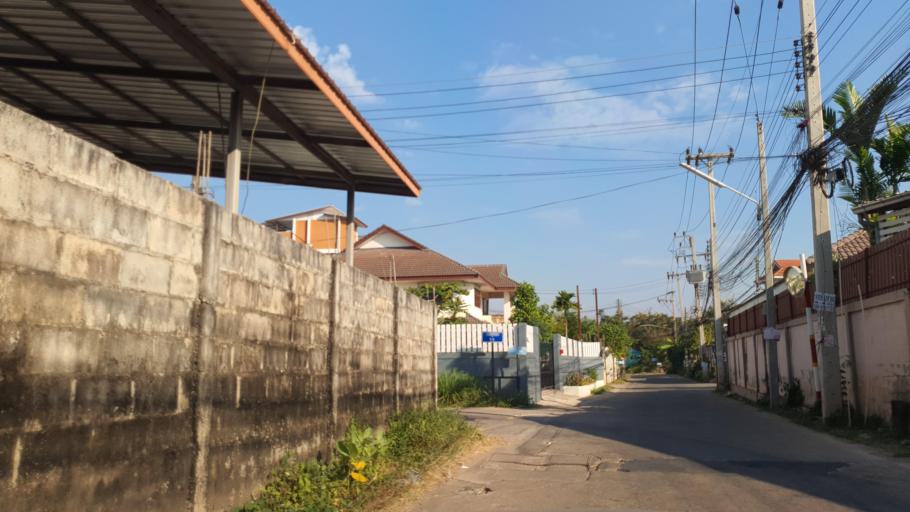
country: TH
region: Khon Kaen
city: Khon Kaen
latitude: 16.4142
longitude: 102.8069
